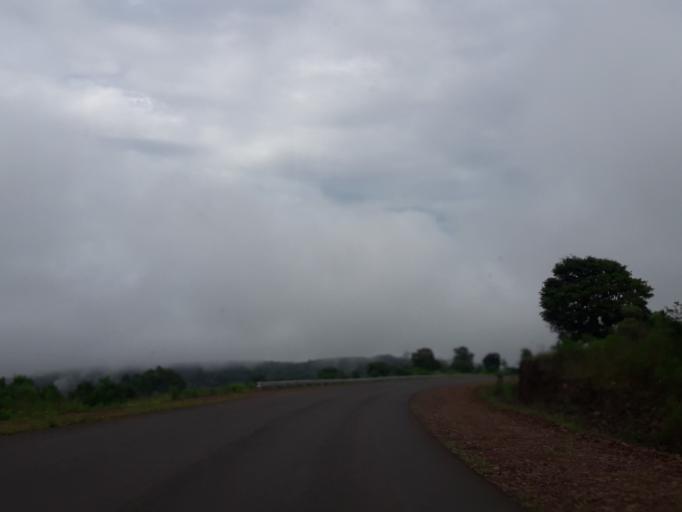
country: AR
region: Misiones
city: Bernardo de Irigoyen
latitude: -26.4197
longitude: -53.8260
